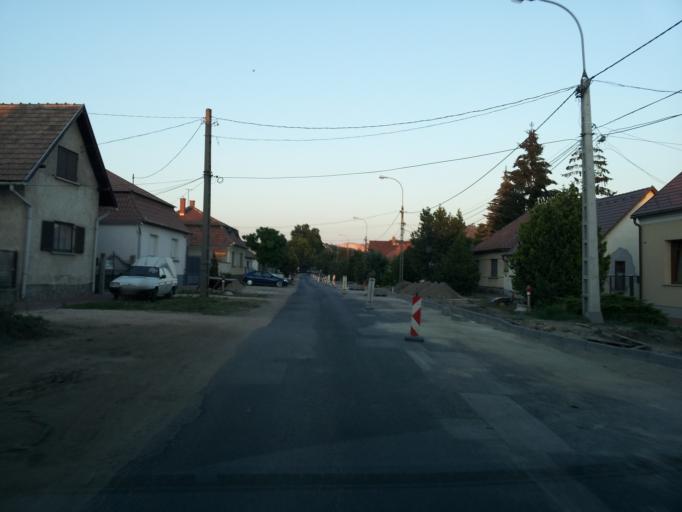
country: HU
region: Komarom-Esztergom
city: Tatabanya
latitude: 47.5720
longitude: 18.4194
